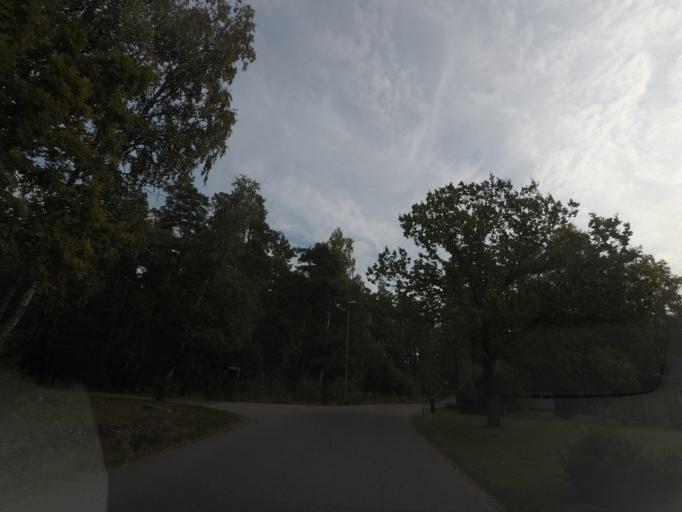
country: SE
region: Soedermanland
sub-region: Eskilstuna Kommun
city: Eskilstuna
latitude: 59.3598
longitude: 16.5560
